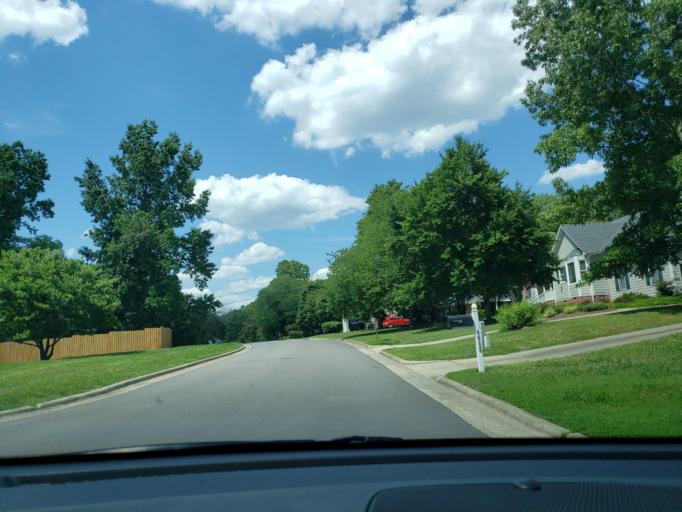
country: US
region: North Carolina
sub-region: Orange County
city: Chapel Hill
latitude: 35.9701
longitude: -78.9877
